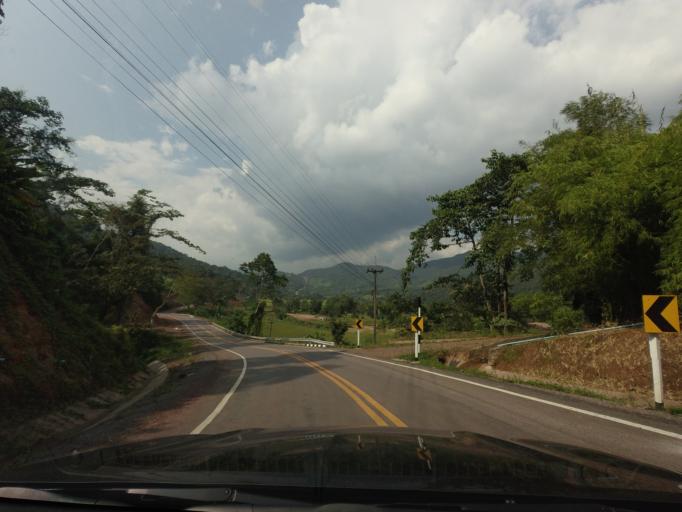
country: TH
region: Nan
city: Bo Kluea
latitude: 19.2172
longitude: 101.1847
